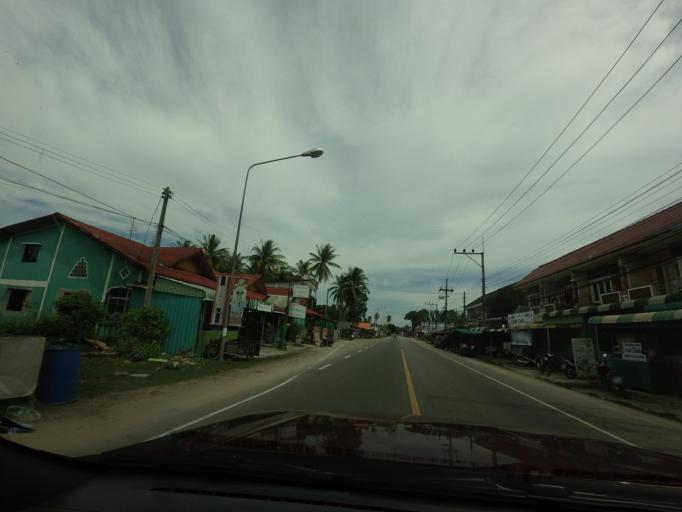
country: TH
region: Narathiwat
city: Tak Bai
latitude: 6.2385
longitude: 102.0830
